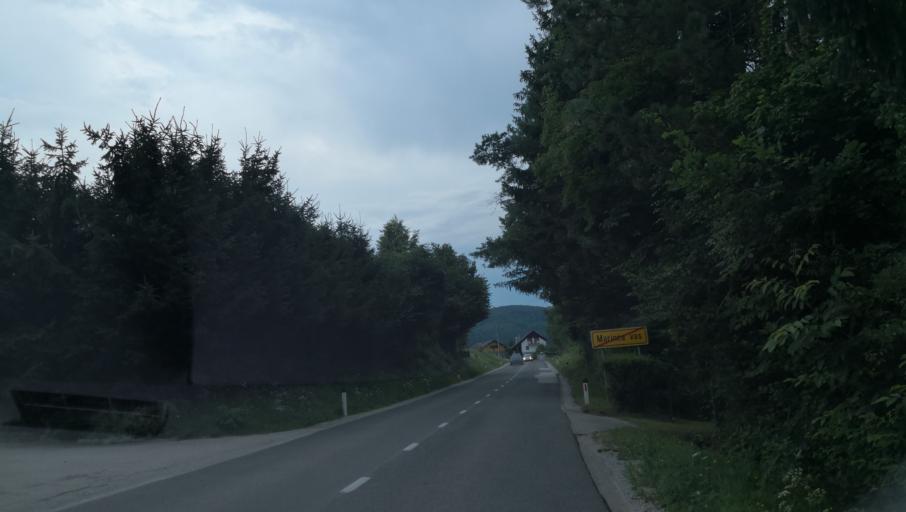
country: SI
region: Ivancna Gorica
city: Ivancna Gorica
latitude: 45.8685
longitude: 14.8256
